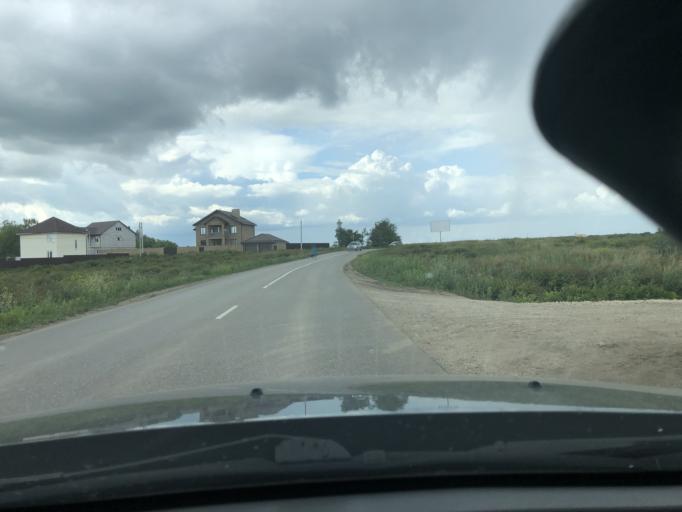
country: RU
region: Tula
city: Kamenetskiy
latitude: 54.0116
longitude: 38.2517
